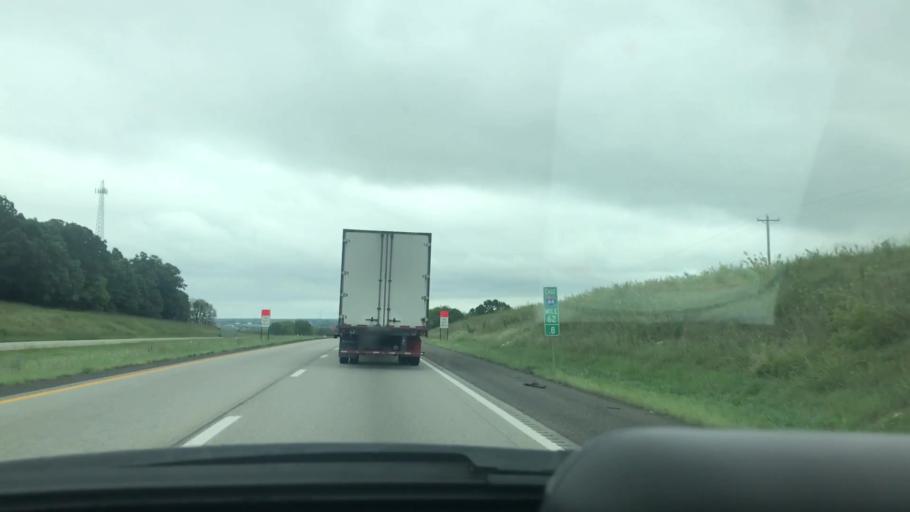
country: US
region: Missouri
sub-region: Greene County
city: Republic
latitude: 37.1858
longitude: -93.5548
